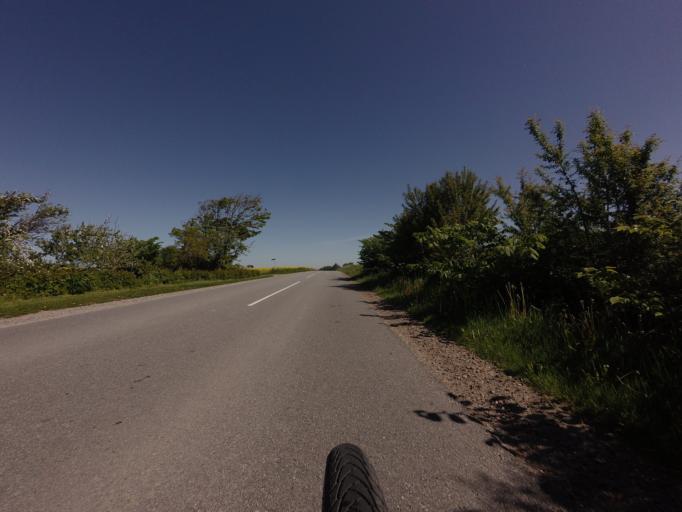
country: DK
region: North Denmark
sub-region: Hjorring Kommune
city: Vra
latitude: 57.4182
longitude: 9.8943
